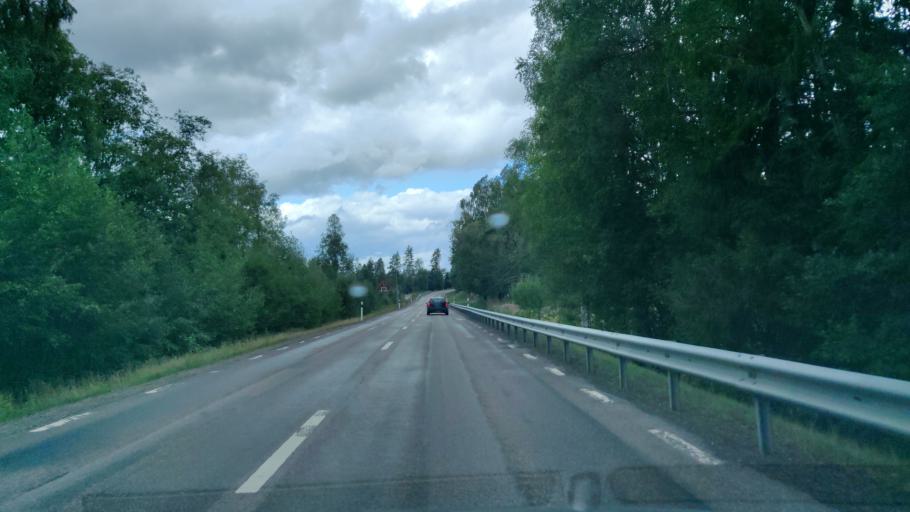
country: SE
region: Vaermland
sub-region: Torsby Kommun
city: Torsby
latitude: 60.5978
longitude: 13.0687
